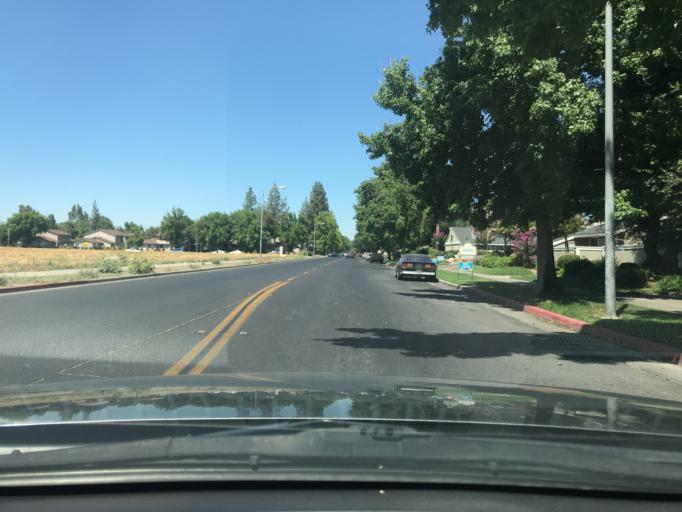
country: US
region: California
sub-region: Merced County
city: Merced
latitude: 37.3235
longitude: -120.4884
